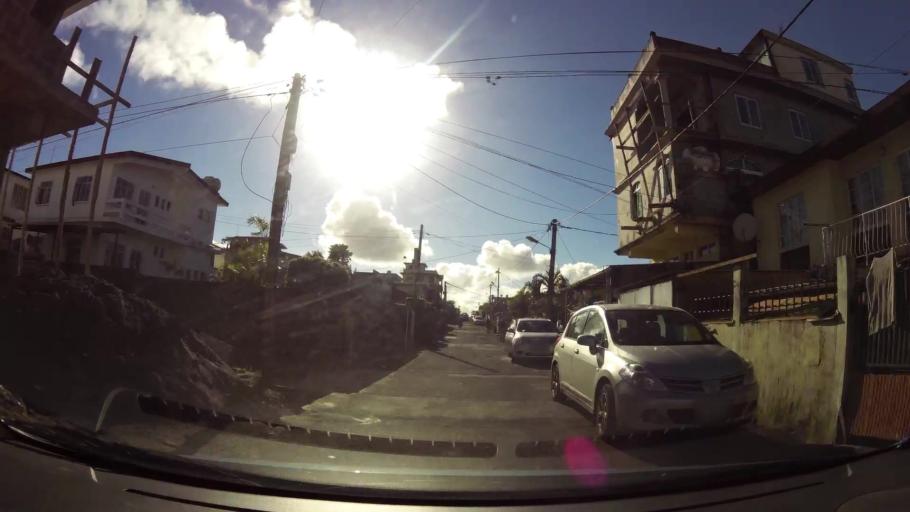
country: MU
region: Plaines Wilhems
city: Curepipe
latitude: -20.3184
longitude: 57.5361
